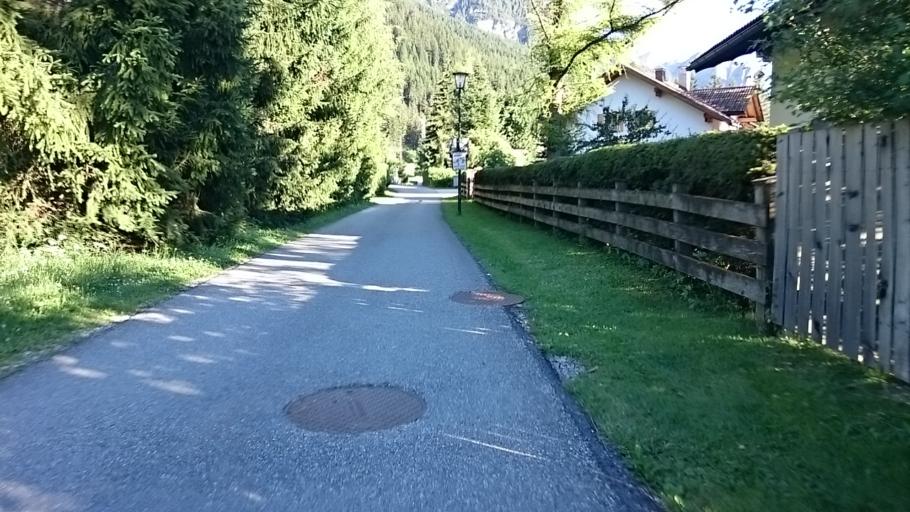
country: IT
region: Trentino-Alto Adige
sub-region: Bolzano
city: Dobbiaco
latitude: 46.7208
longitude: 12.2217
